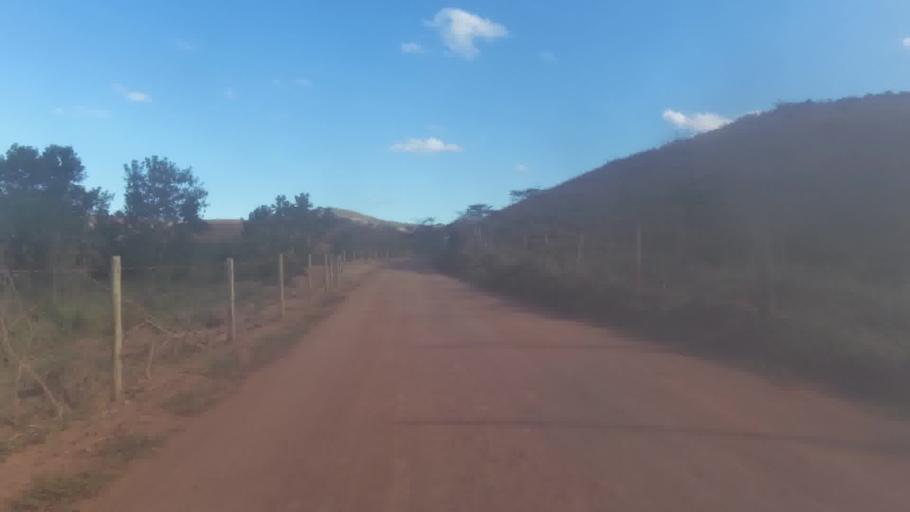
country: BR
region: Espirito Santo
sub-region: Mimoso Do Sul
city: Mimoso do Sul
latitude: -21.0783
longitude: -41.1459
